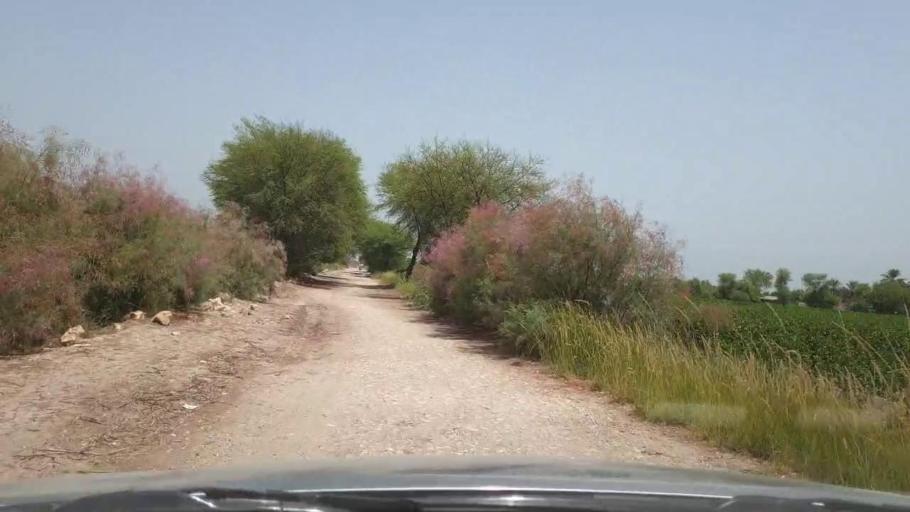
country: PK
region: Sindh
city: Pano Aqil
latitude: 27.8679
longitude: 69.1877
